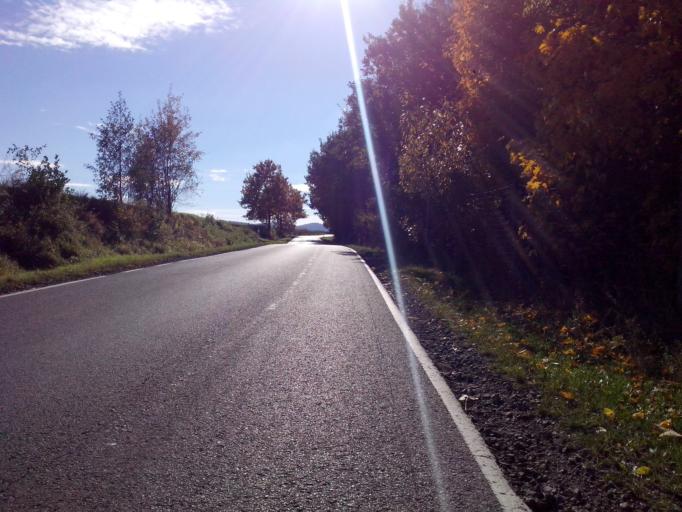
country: PL
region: Subcarpathian Voivodeship
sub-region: Powiat strzyzowski
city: Jawornik
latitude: 49.7997
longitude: 21.8634
